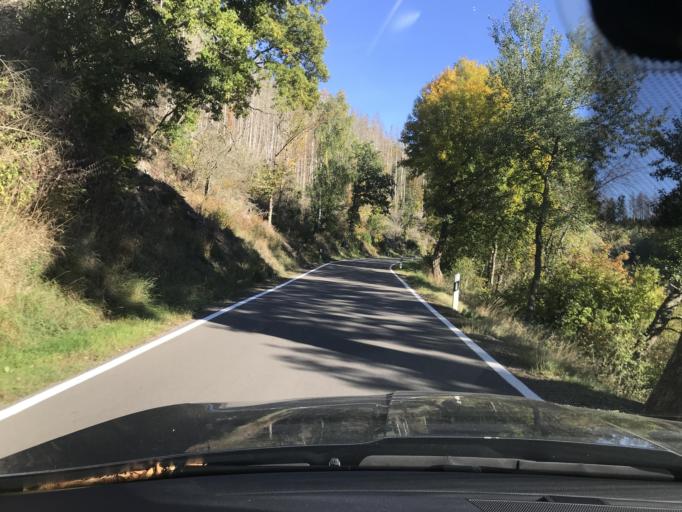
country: DE
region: Saxony-Anhalt
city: Friedrichsbrunn
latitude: 51.6878
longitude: 10.9661
